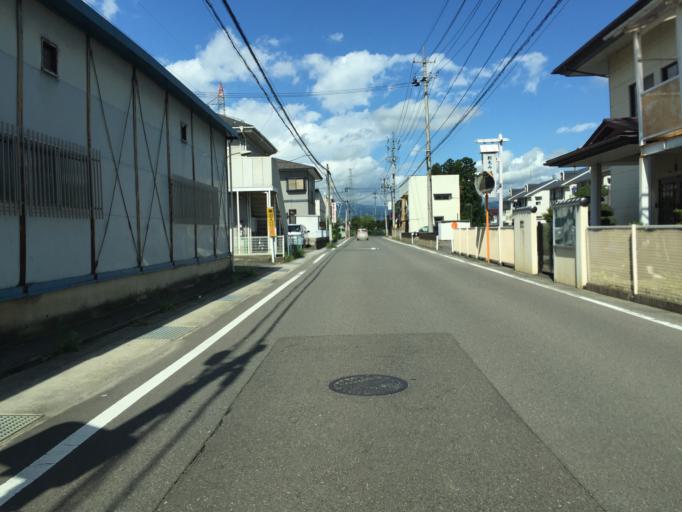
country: JP
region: Fukushima
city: Fukushima-shi
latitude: 37.7271
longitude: 140.4503
